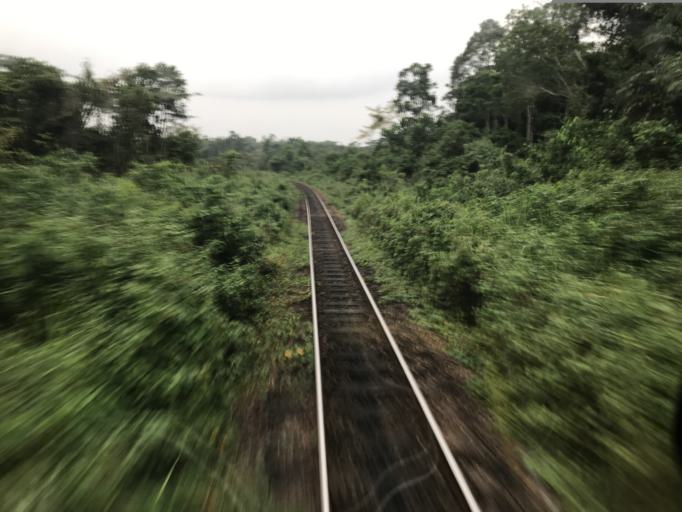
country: CM
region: Littoral
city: Edea
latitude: 3.9224
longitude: 10.1087
